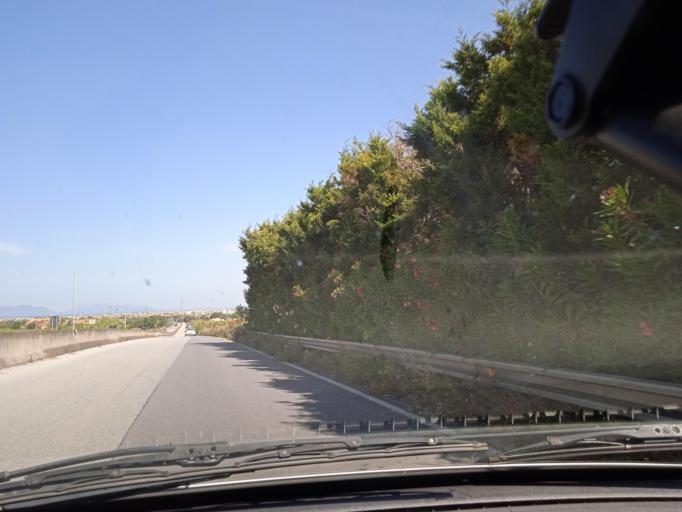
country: IT
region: Sicily
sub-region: Messina
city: San Filippo del Mela
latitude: 38.1877
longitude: 15.2631
